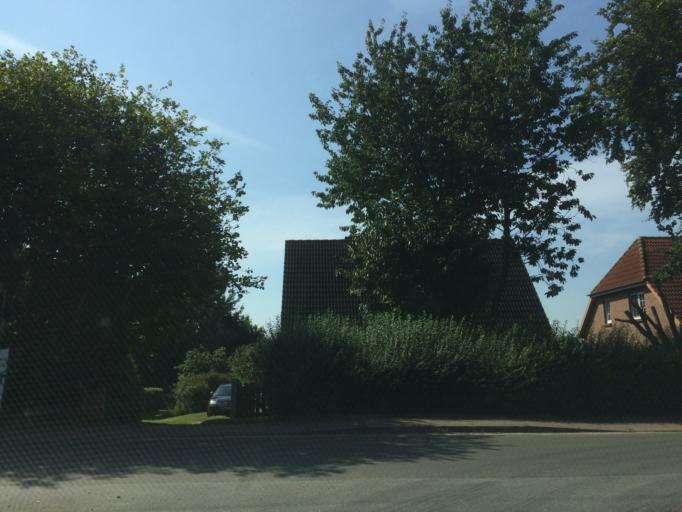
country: DE
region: Schleswig-Holstein
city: Neudorf-Bornstein
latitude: 54.4186
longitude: 9.9219
